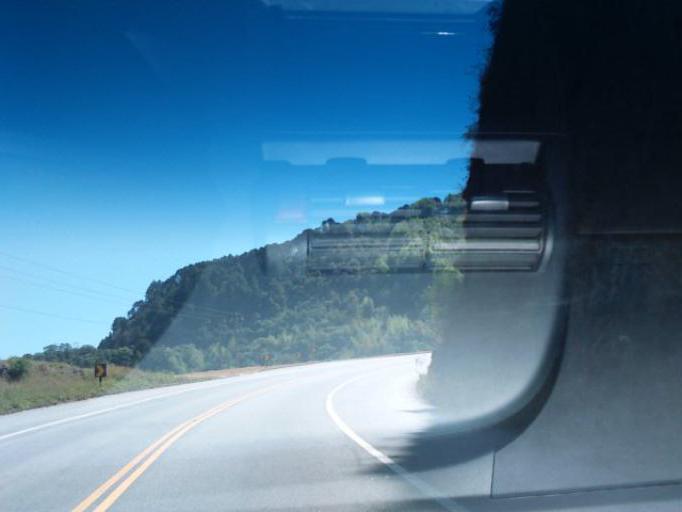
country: BR
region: Sao Paulo
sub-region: Campos Do Jordao
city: Campos do Jordao
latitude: -22.7815
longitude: -45.6110
